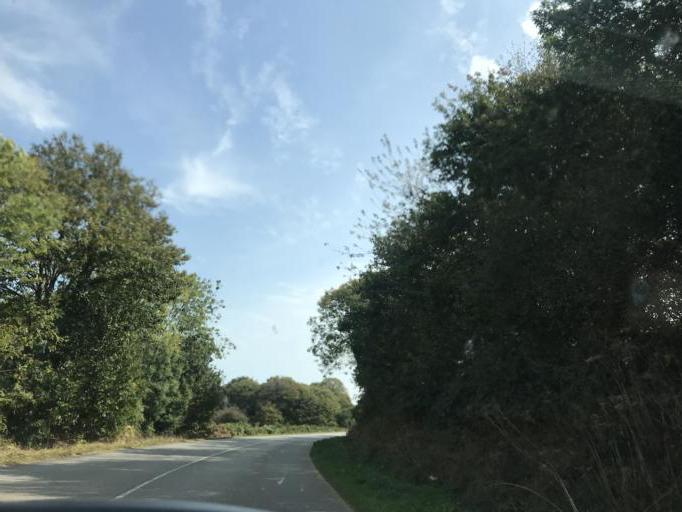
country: FR
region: Brittany
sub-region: Departement du Finistere
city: Le Faou
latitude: 48.2860
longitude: -4.1492
